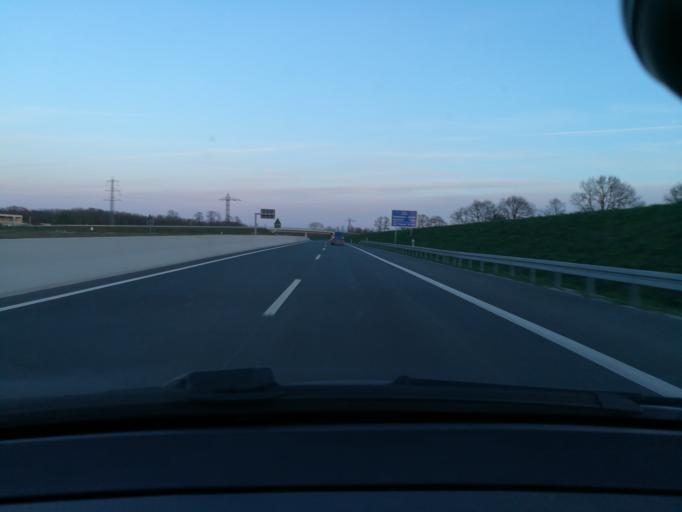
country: DE
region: North Rhine-Westphalia
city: Halle
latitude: 52.0360
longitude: 8.3460
